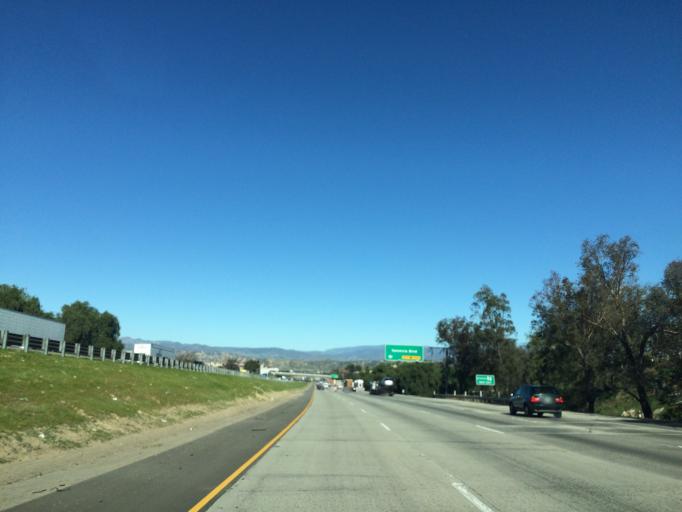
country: US
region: California
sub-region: Los Angeles County
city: Santa Clarita
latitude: 34.4002
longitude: -118.5727
